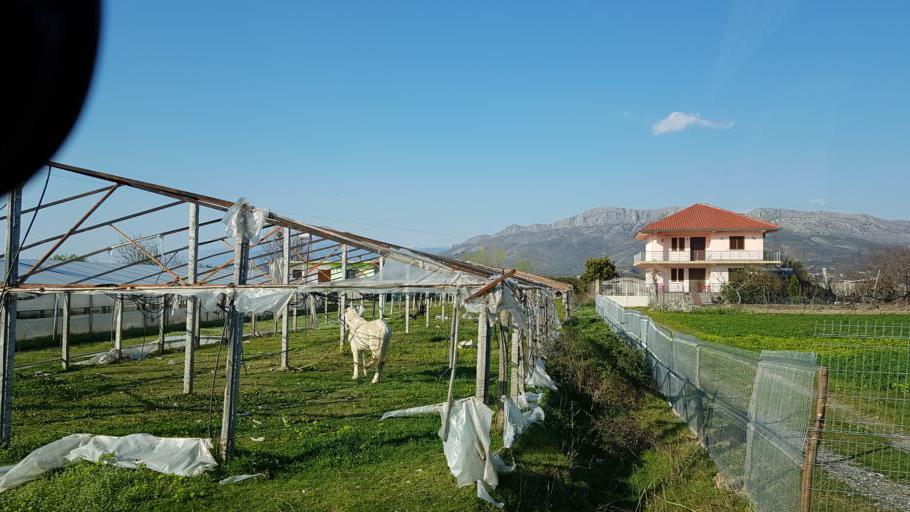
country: AL
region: Shkoder
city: Vukatane
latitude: 41.9926
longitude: 19.5622
